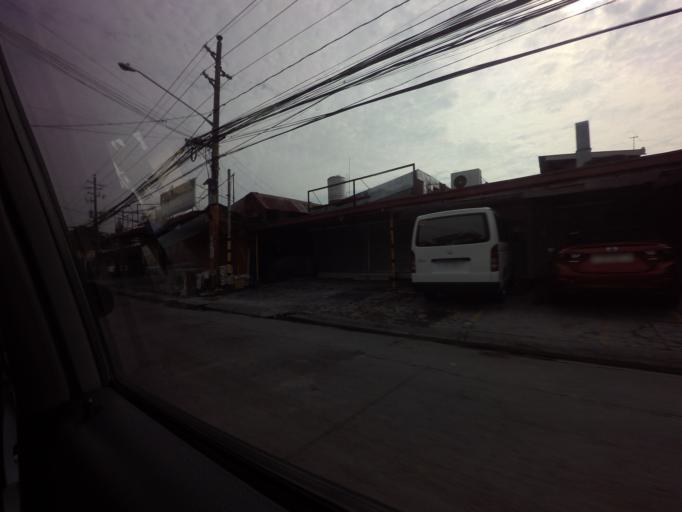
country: PH
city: Sambayanihan People's Village
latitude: 14.4489
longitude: 121.0193
